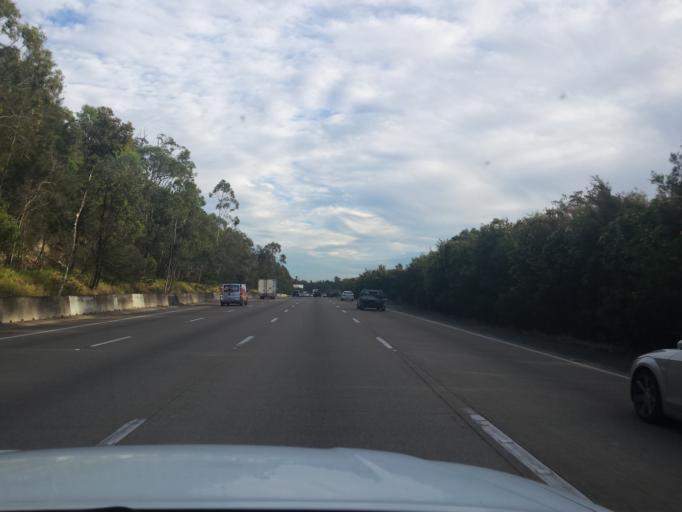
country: AU
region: Queensland
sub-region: Gold Coast
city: Oxenford
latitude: -27.8406
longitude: 153.3036
